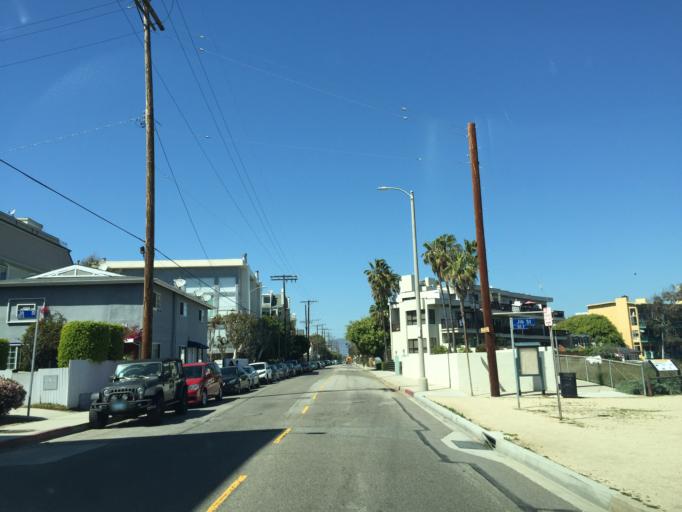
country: US
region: California
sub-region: Los Angeles County
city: Marina del Rey
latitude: 33.9742
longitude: -118.4613
